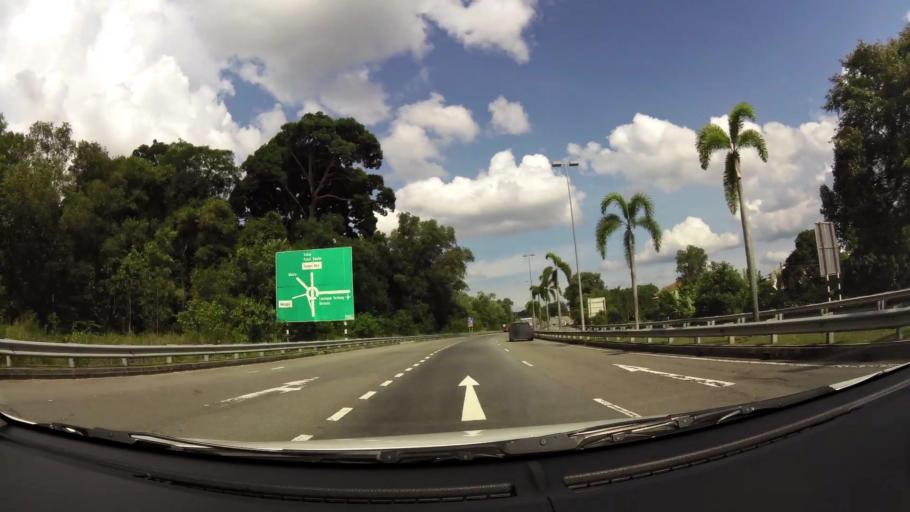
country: BN
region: Brunei and Muara
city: Bandar Seri Begawan
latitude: 4.9527
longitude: 114.9597
